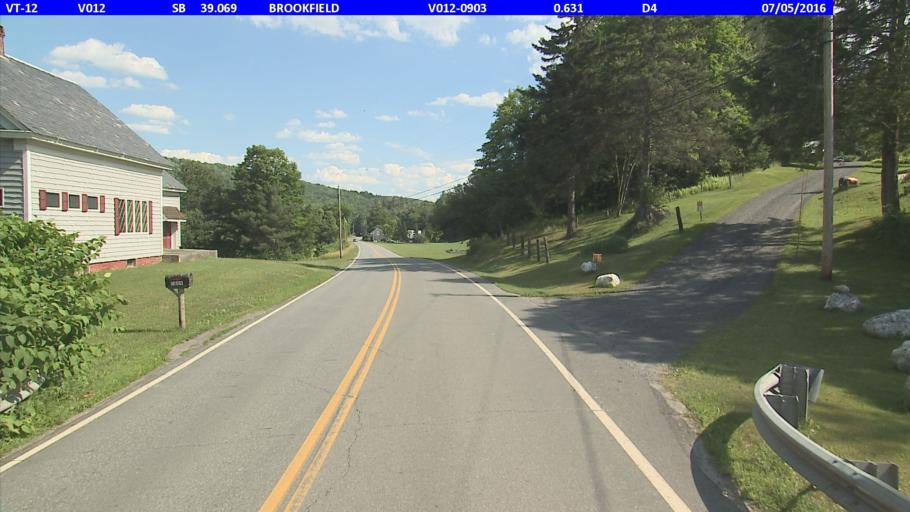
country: US
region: Vermont
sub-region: Orange County
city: Randolph
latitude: 44.0136
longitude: -72.6582
